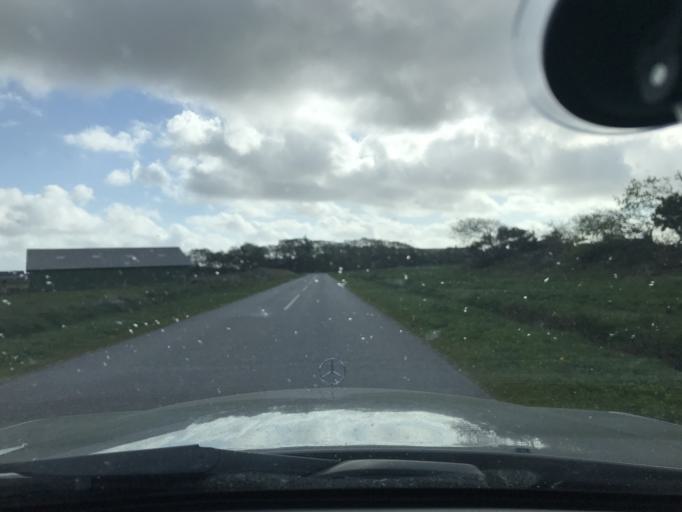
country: DE
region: Schleswig-Holstein
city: List
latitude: 55.1796
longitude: 8.5582
